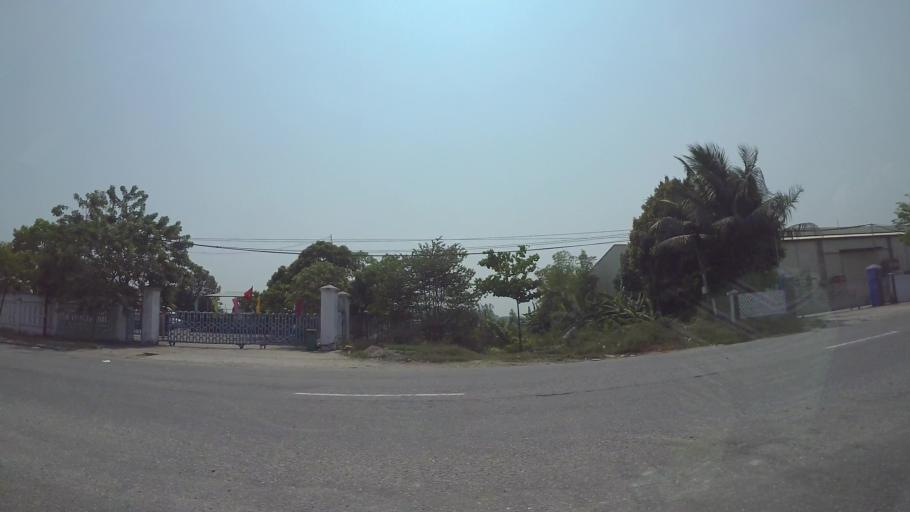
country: VN
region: Da Nang
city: Cam Le
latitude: 15.9914
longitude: 108.1955
